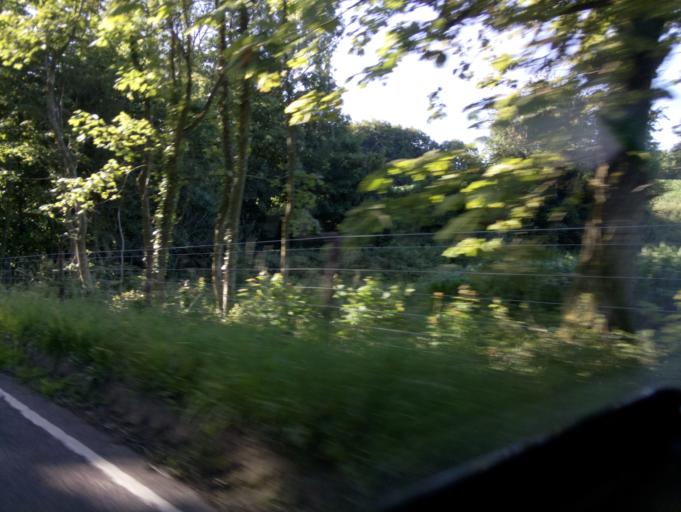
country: GB
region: Wales
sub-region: Monmouthshire
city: Chepstow
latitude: 51.6609
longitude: -2.7355
